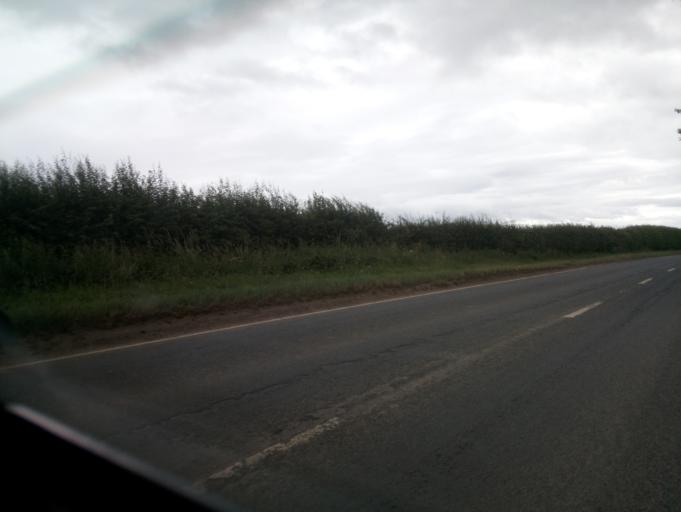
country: GB
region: England
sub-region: Worcestershire
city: Kempsey
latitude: 52.1496
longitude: -2.2159
